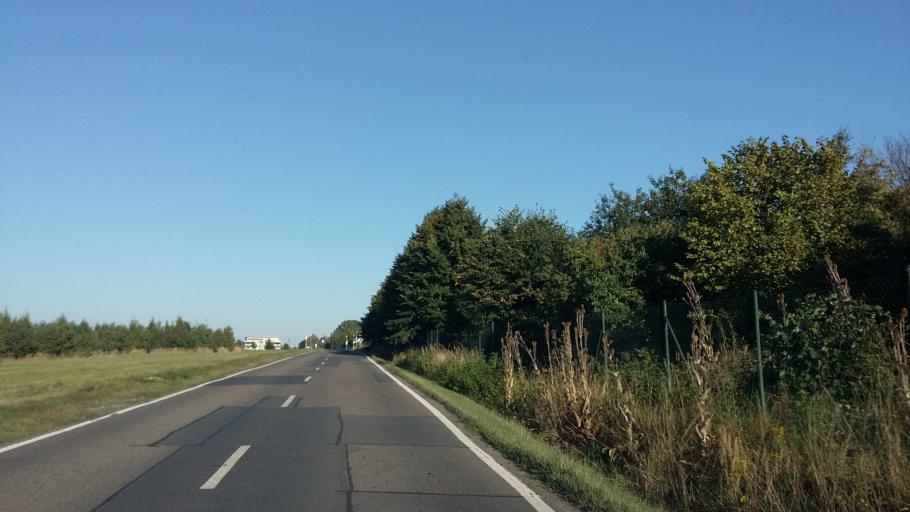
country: CZ
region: Praha
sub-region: Praha 18
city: Letnany
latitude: 50.1356
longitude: 14.5313
